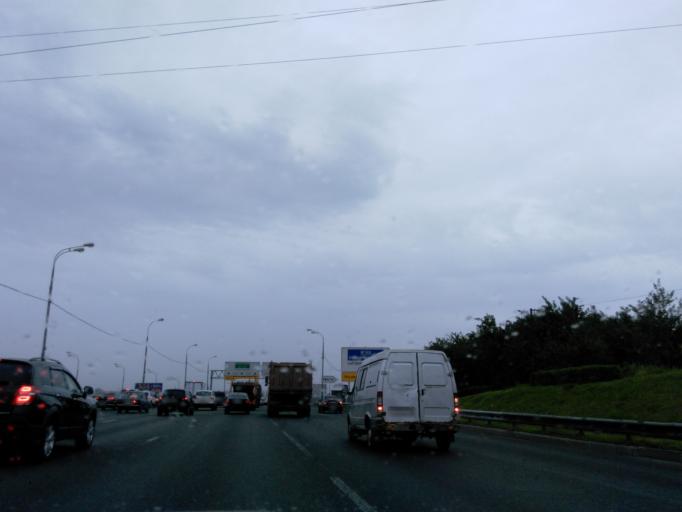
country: RU
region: Moscow
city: Strogino
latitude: 55.8364
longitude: 37.3958
